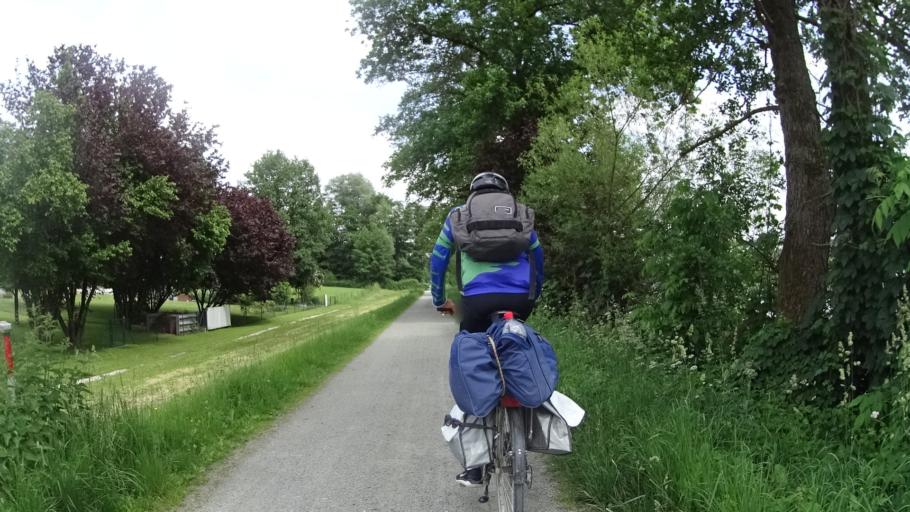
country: DE
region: Bavaria
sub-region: Lower Bavaria
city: Tiefenbach
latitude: 48.6007
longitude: 13.3627
